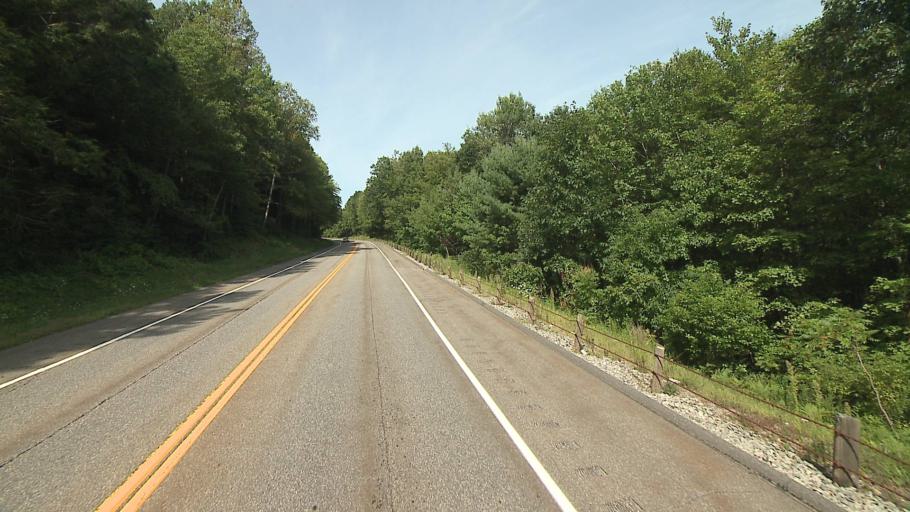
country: US
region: Connecticut
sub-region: Litchfield County
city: Torrington
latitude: 41.7615
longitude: -73.1435
